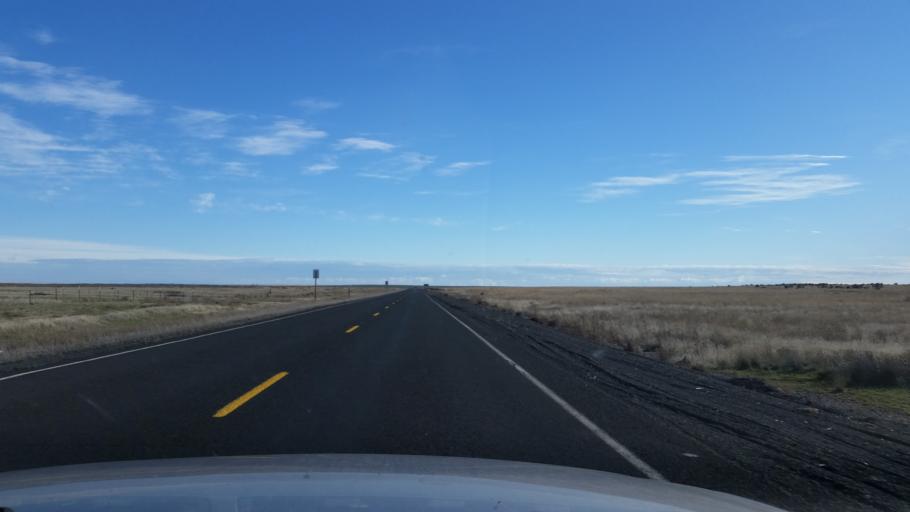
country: US
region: Washington
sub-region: Grant County
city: Moses Lake North
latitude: 47.3654
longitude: -118.9778
